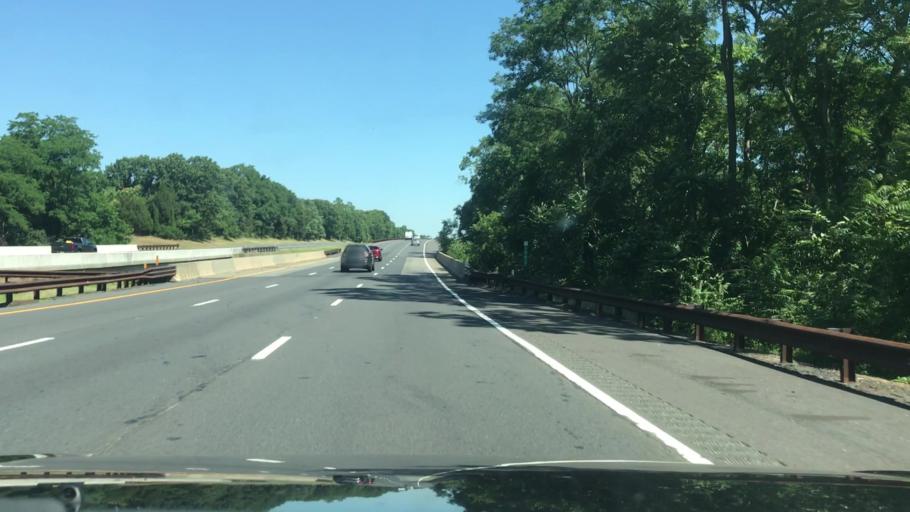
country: US
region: New Jersey
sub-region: Monmouth County
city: Tinton Falls
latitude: 40.3156
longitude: -74.0966
